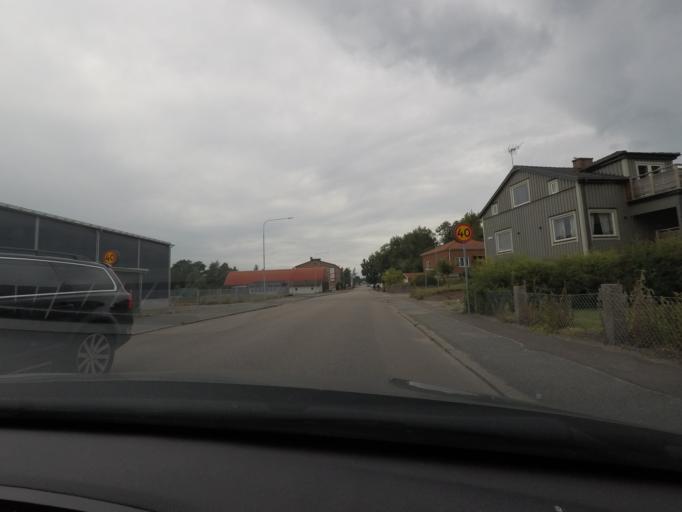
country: SE
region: Skane
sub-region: Osby Kommun
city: Osby
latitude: 56.3807
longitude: 13.9869
